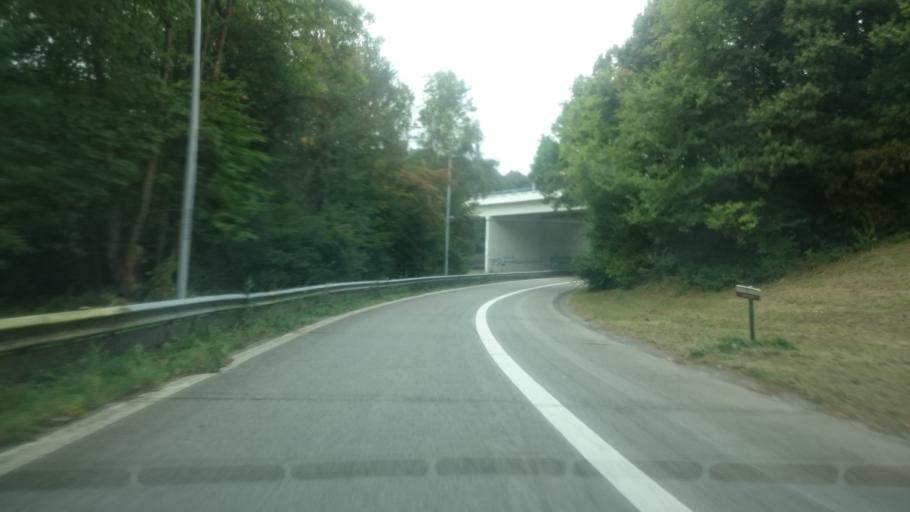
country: BE
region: Wallonia
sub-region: Province de Namur
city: Namur
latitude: 50.5227
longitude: 4.8821
